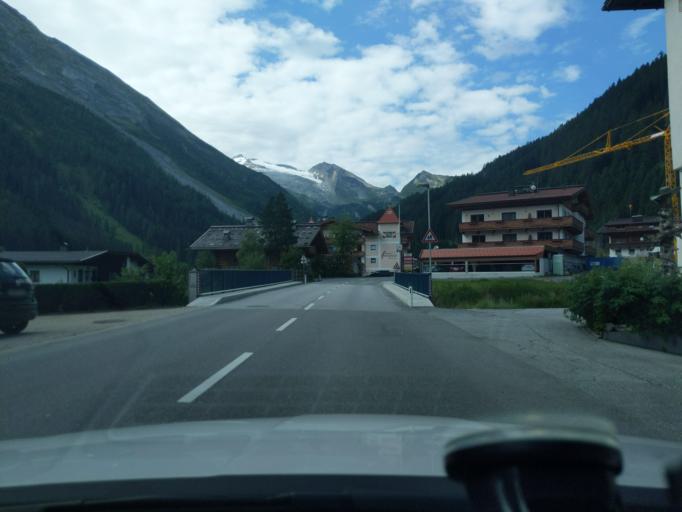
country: AT
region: Tyrol
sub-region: Politischer Bezirk Innsbruck Land
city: Schmirn
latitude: 47.1274
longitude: 11.6973
